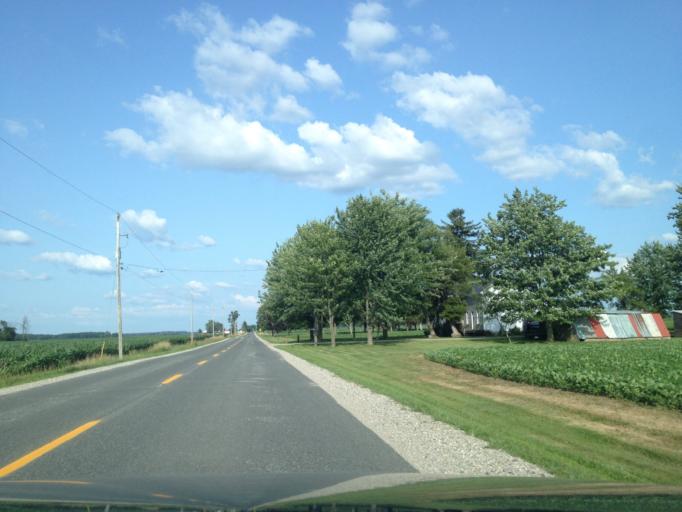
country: CA
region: Ontario
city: Ingersoll
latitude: 42.9659
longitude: -80.7433
